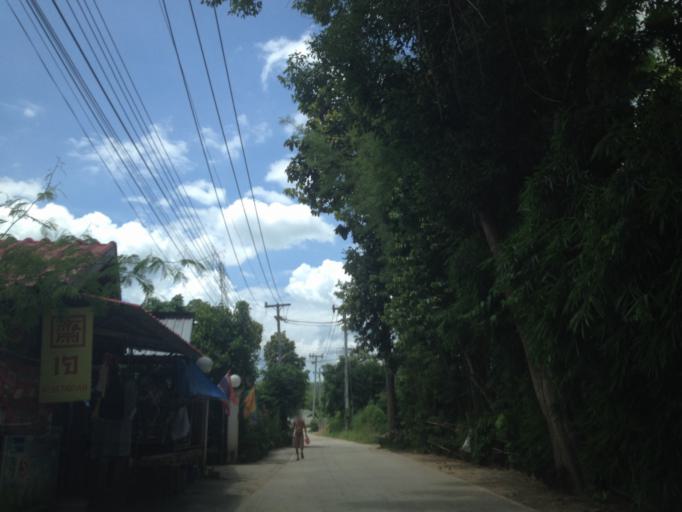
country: TH
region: Chiang Mai
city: Hang Dong
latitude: 18.6914
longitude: 98.8899
